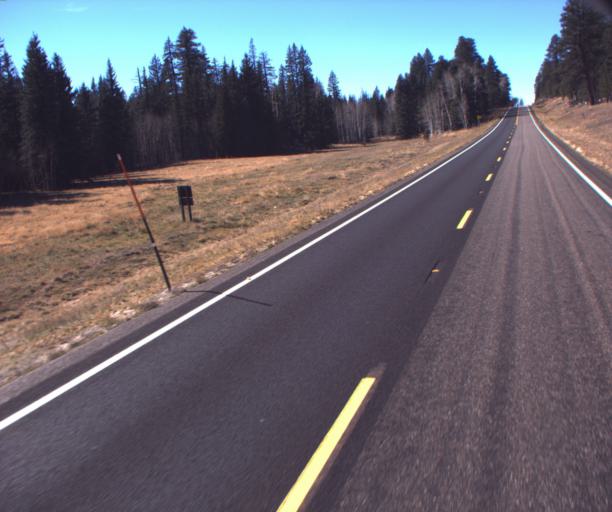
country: US
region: Arizona
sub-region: Coconino County
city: Grand Canyon
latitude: 36.5427
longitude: -112.1663
